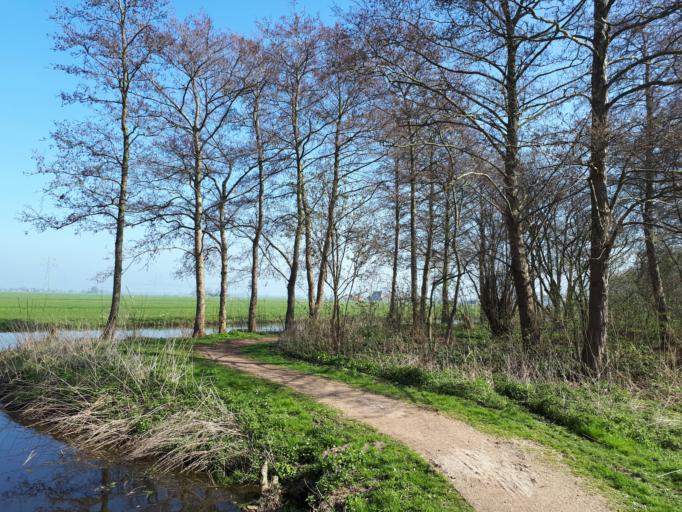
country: NL
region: South Holland
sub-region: Gemeente Krimpen aan den IJssel
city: Krimpen aan den IJssel
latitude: 51.9325
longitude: 4.6437
